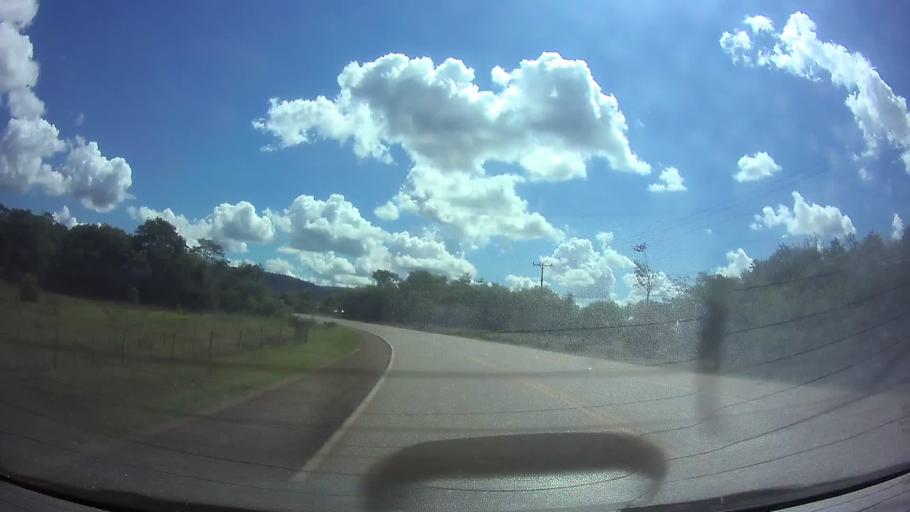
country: PY
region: Guaira
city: Itape
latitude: -25.9142
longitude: -56.6991
